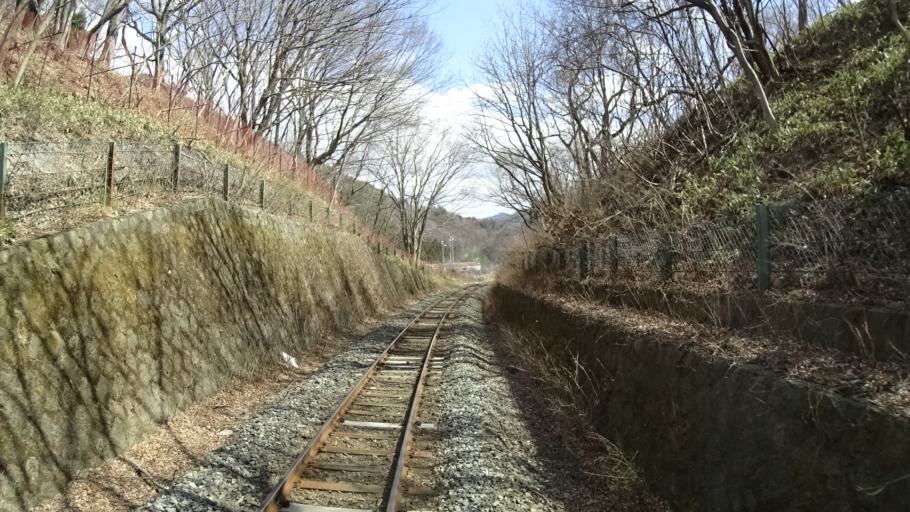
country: JP
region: Iwate
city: Kamaishi
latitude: 39.2544
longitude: 141.7497
